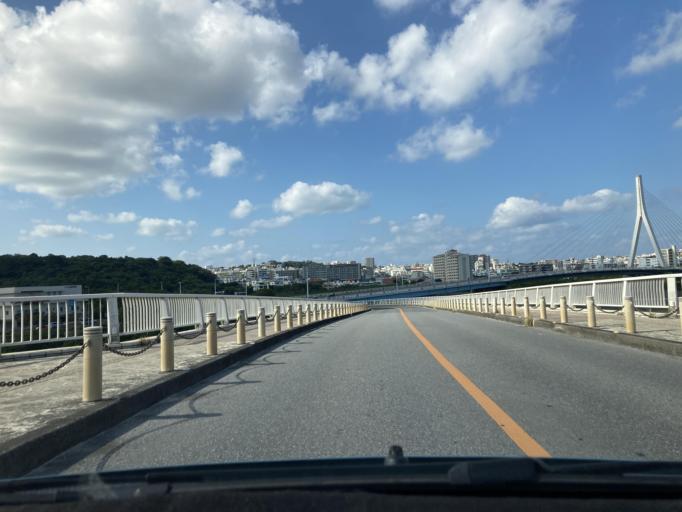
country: JP
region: Okinawa
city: Tomigusuku
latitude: 26.1949
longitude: 127.6879
